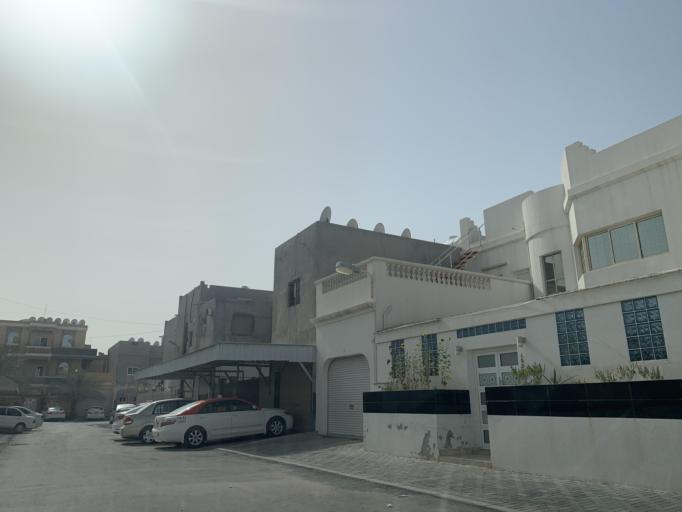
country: BH
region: Northern
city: Madinat `Isa
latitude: 26.1607
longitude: 50.5200
